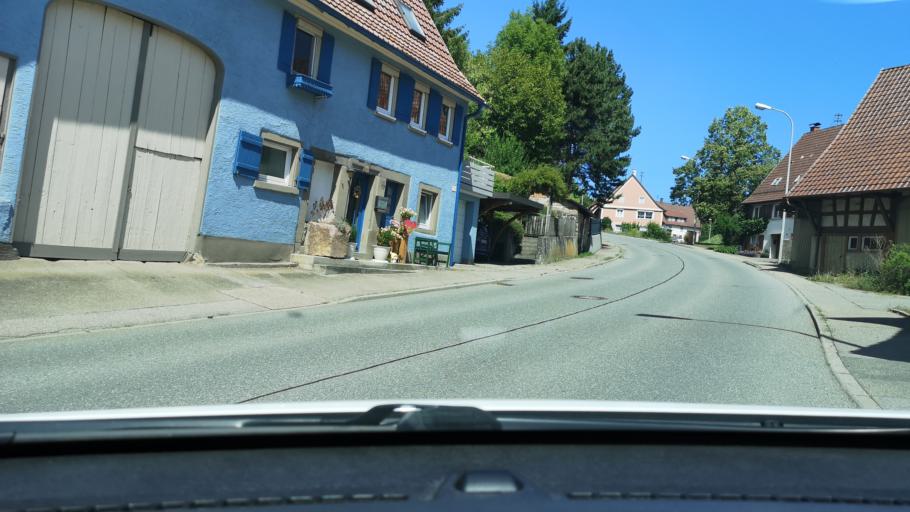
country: DE
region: Baden-Wuerttemberg
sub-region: Freiburg Region
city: Vohringen
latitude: 48.3469
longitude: 8.6842
